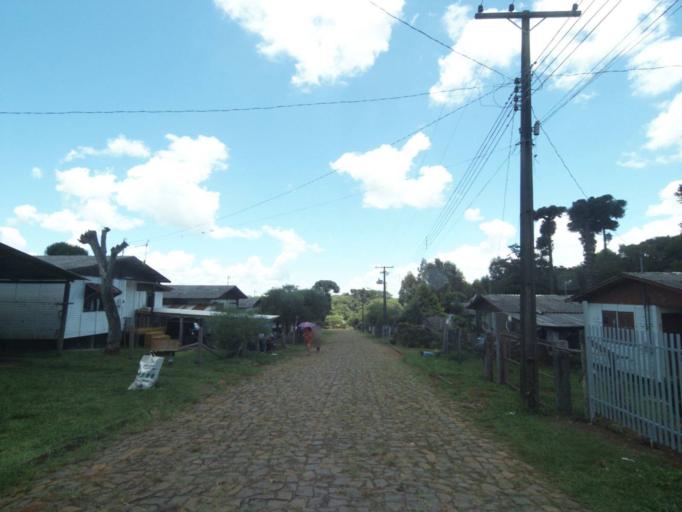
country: BR
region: Parana
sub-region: Pinhao
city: Pinhao
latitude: -25.7876
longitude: -52.0860
